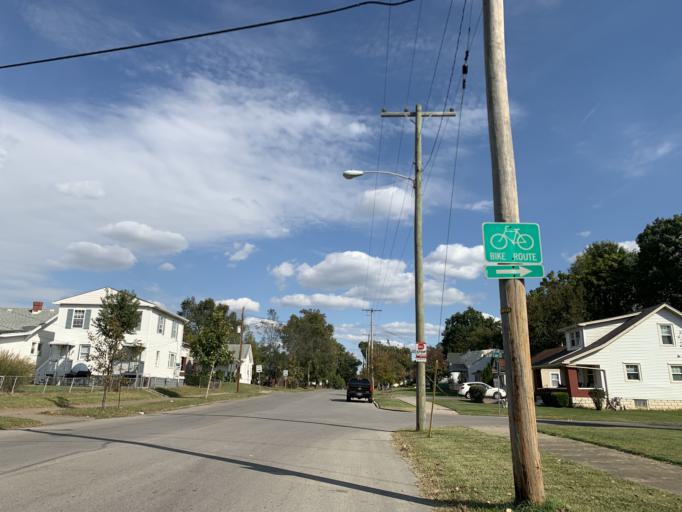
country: US
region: Indiana
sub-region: Floyd County
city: New Albany
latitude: 38.2465
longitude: -85.8161
